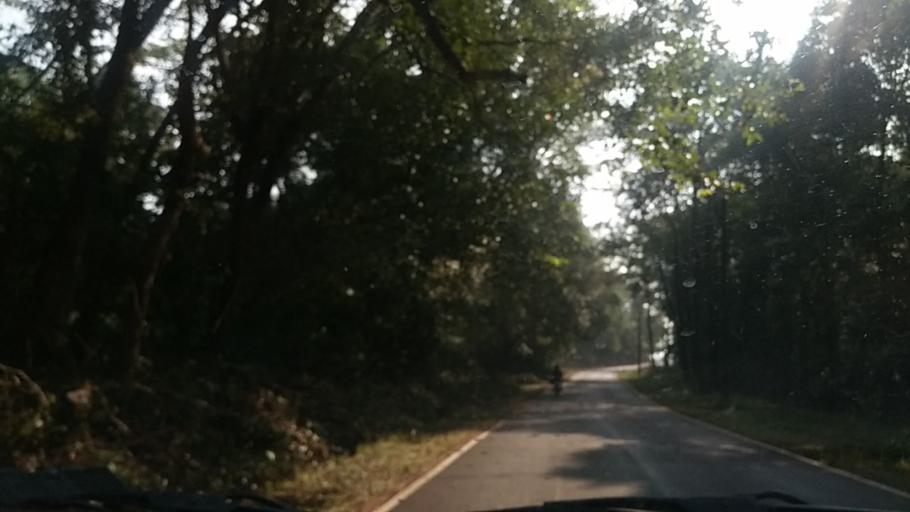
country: IN
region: Goa
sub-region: South Goa
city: Sanguem
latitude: 15.2178
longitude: 74.2012
